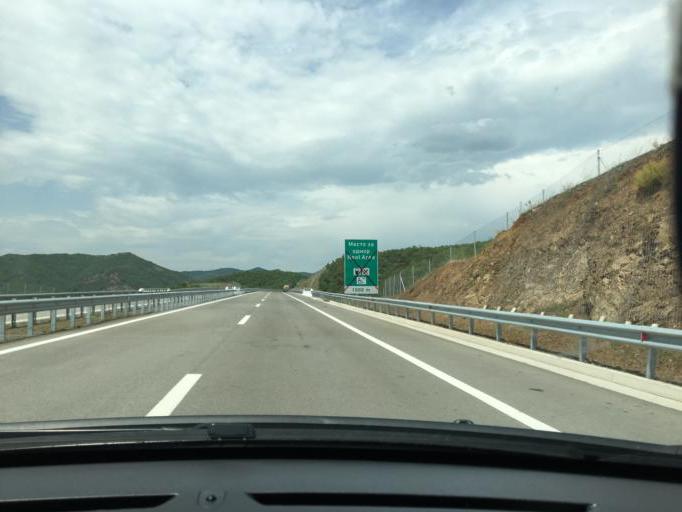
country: MK
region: Gevgelija
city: Miravci
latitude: 41.3148
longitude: 22.4138
